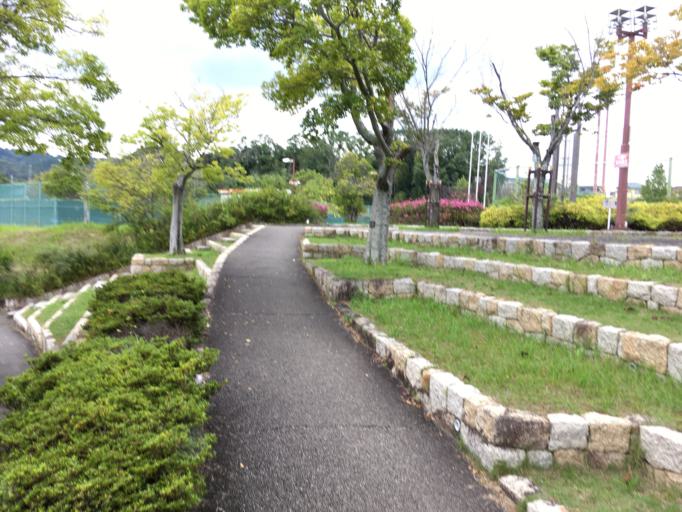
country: JP
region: Nara
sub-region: Ikoma-shi
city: Ikoma
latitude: 34.6230
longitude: 135.7015
